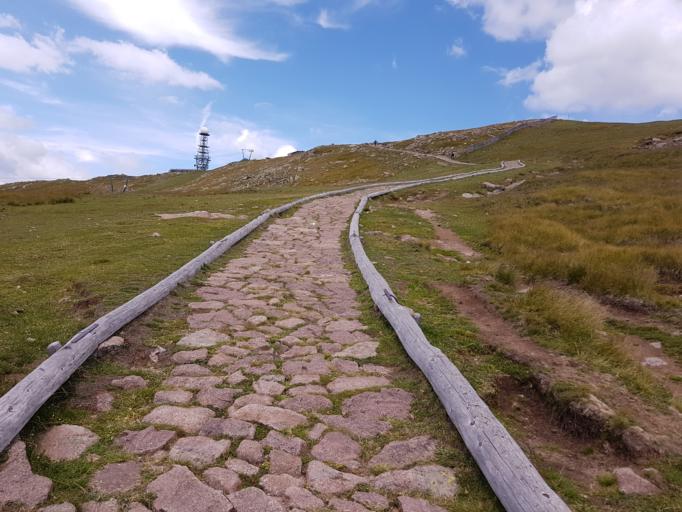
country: IT
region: Trentino-Alto Adige
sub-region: Bolzano
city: Barbiano
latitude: 46.6114
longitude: 11.4608
